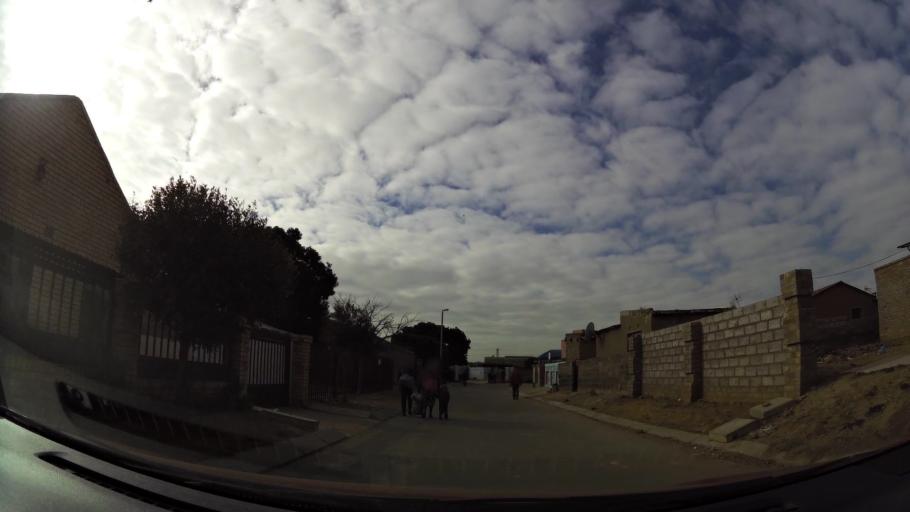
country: ZA
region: Gauteng
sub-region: City of Johannesburg Metropolitan Municipality
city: Modderfontein
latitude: -26.0450
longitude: 28.1839
